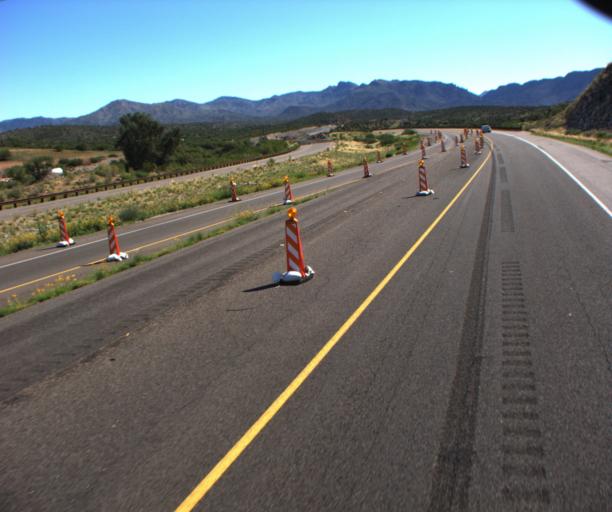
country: US
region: Arizona
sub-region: Pinal County
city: Superior
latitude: 33.2765
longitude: -111.1769
